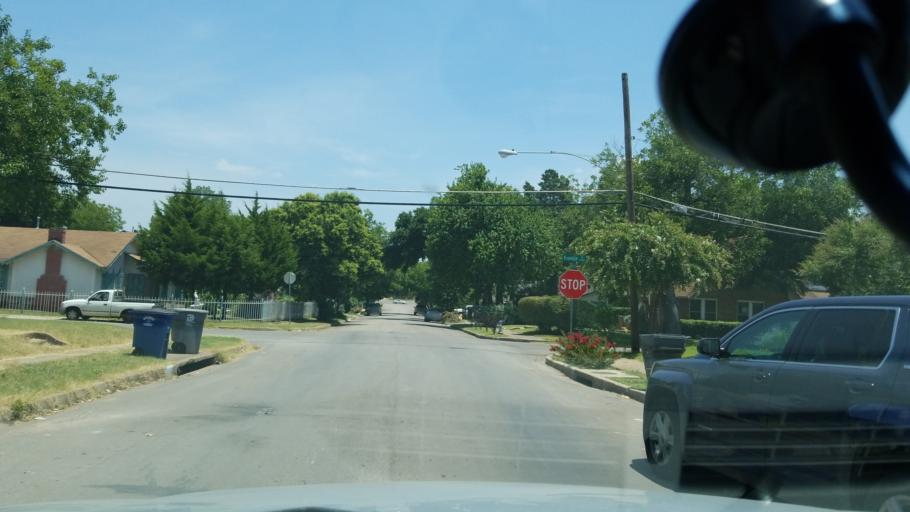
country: US
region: Texas
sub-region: Dallas County
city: Cockrell Hill
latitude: 32.7302
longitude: -96.8596
